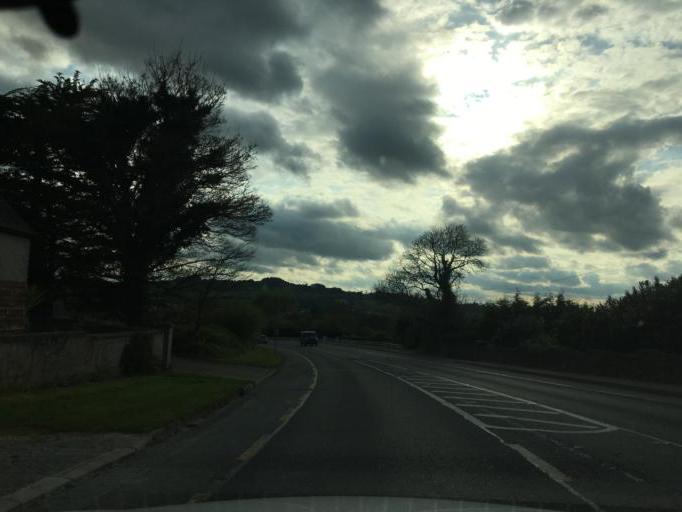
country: IE
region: Leinster
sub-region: Loch Garman
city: Loch Garman
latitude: 52.3405
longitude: -6.5073
